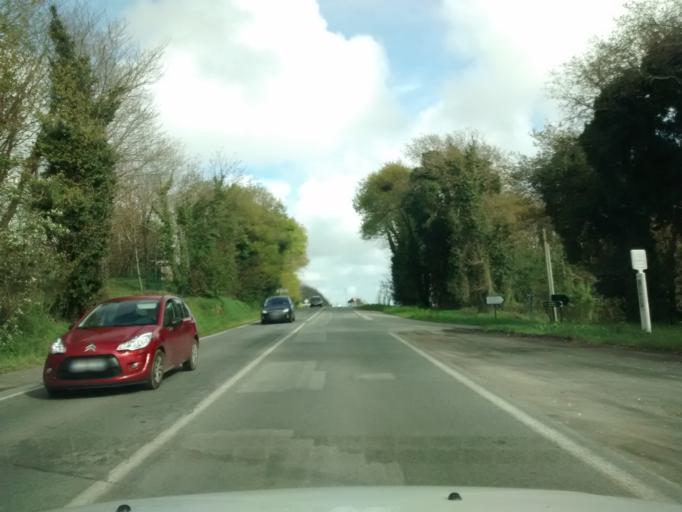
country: FR
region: Brittany
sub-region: Departement du Morbihan
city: Queven
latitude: 47.7773
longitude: -3.4244
